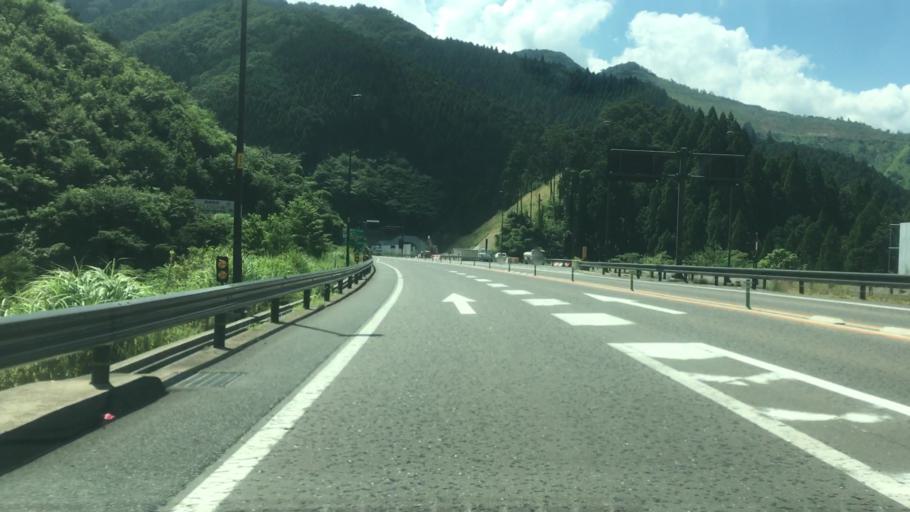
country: JP
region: Tottori
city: Tottori
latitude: 35.2853
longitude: 134.2240
